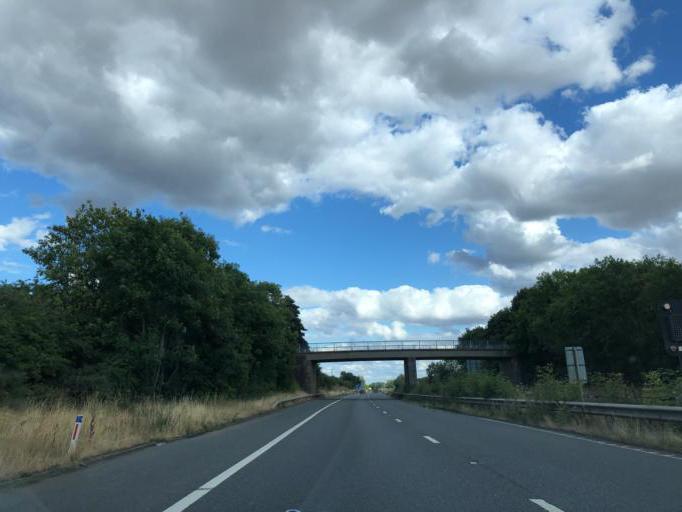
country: GB
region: England
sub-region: Warwickshire
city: Dunchurch
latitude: 52.3389
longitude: -1.3148
